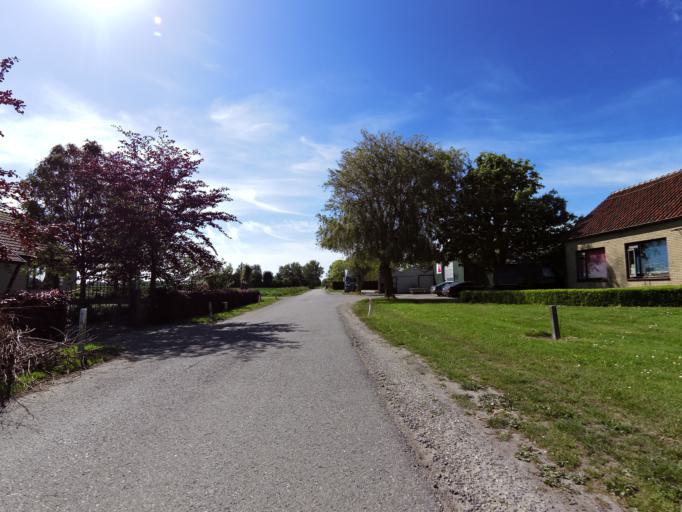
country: NL
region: South Holland
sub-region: Gemeente Brielle
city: Brielle
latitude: 51.8903
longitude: 4.1350
